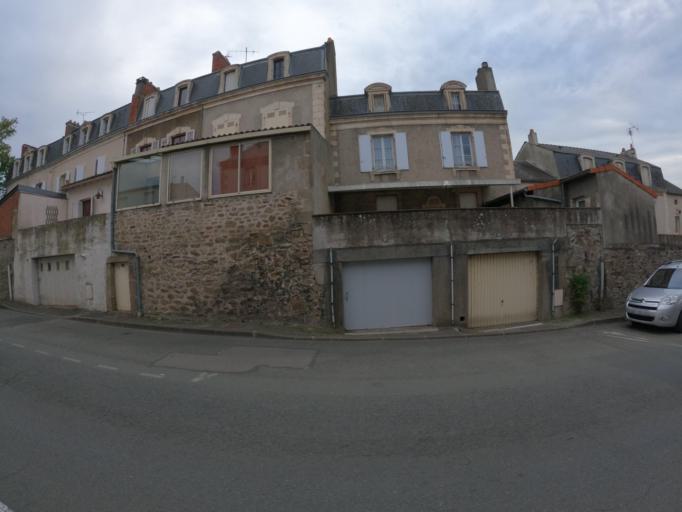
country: FR
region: Poitou-Charentes
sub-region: Departement des Deux-Sevres
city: Parthenay
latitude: 46.6498
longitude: -0.2466
